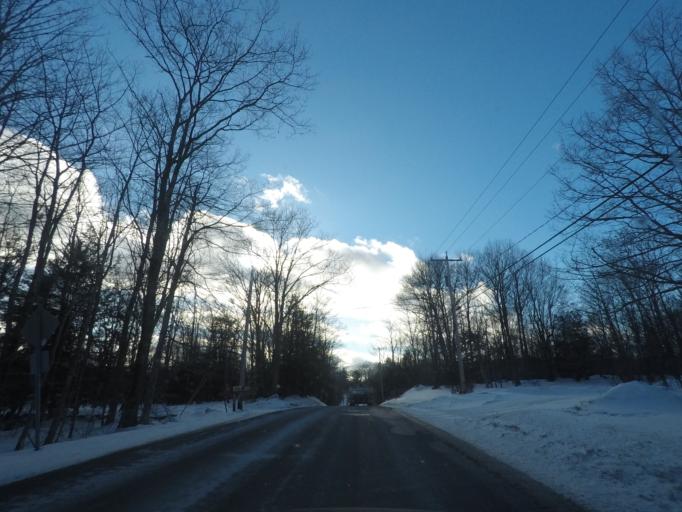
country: US
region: New York
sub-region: Rensselaer County
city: Hoosick Falls
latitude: 42.7829
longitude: -73.4100
